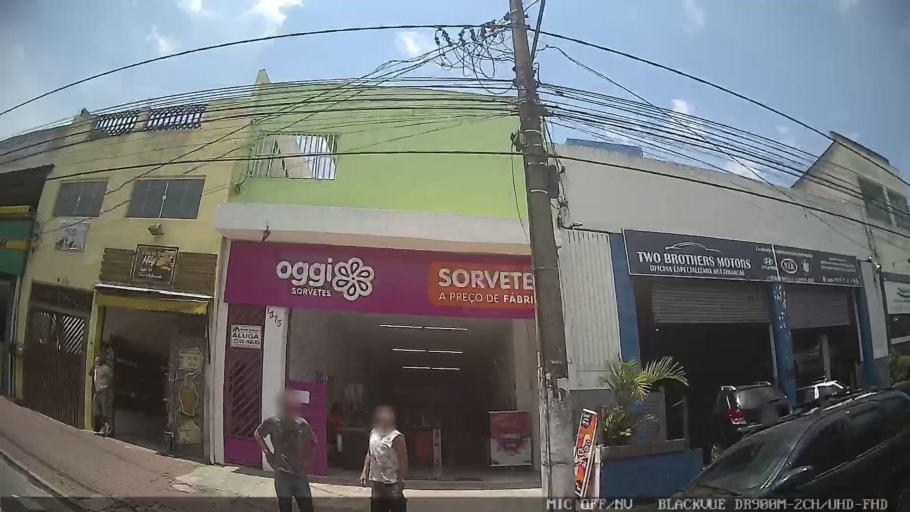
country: BR
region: Sao Paulo
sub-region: Ferraz De Vasconcelos
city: Ferraz de Vasconcelos
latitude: -23.5557
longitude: -46.3859
